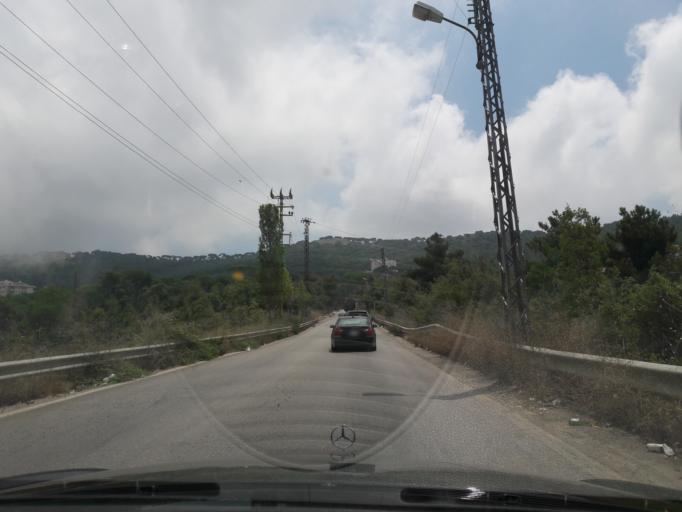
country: LB
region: Mont-Liban
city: Djounie
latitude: 33.9164
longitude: 35.6859
